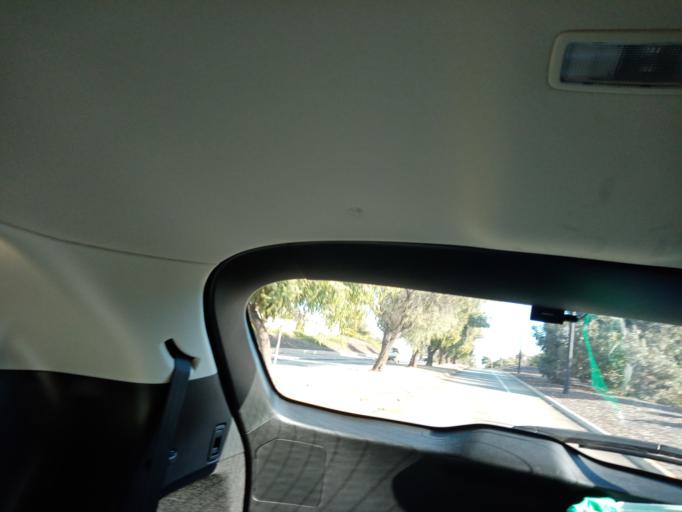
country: AU
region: Western Australia
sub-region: City of Cockburn
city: Beeliar
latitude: -32.1306
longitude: 115.8116
